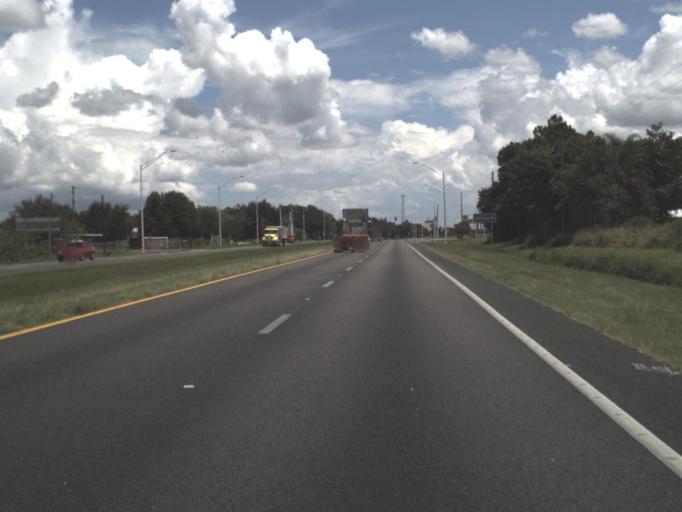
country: US
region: Florida
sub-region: Polk County
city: Wahneta
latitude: 27.9162
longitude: -81.7215
